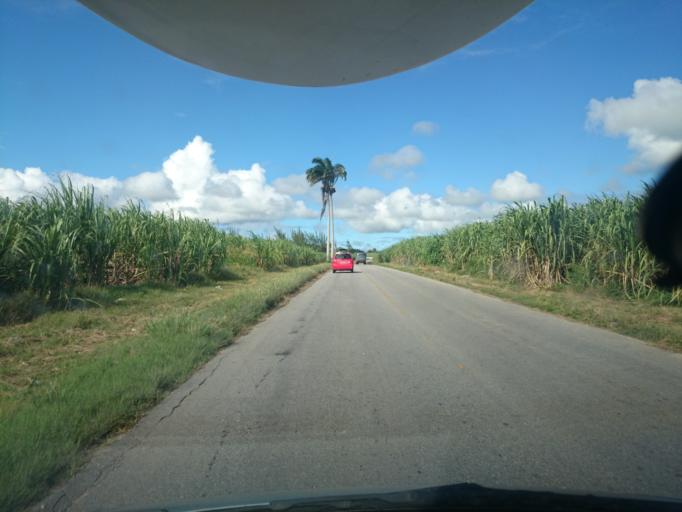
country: BB
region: Christ Church
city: Oistins
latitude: 13.0831
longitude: -59.5298
